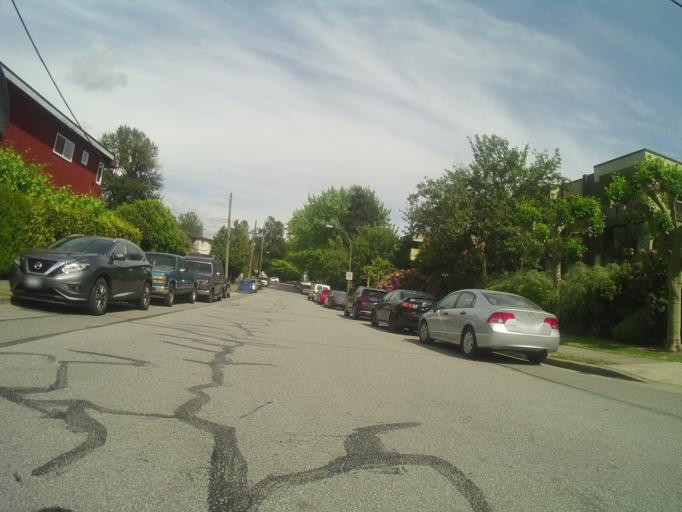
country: CA
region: British Columbia
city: Vancouver
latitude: 49.2642
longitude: -123.0755
